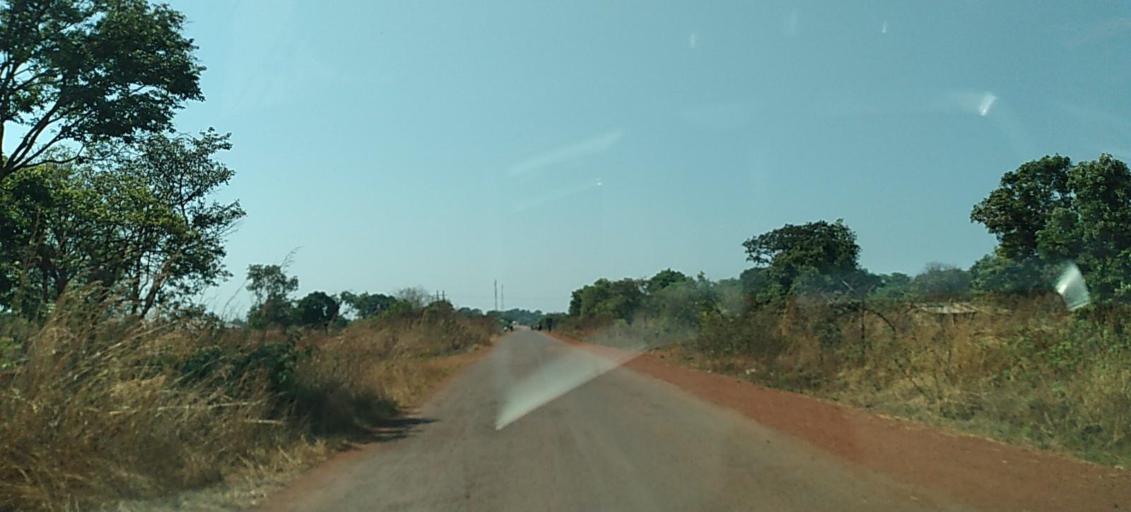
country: ZM
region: North-Western
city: Solwezi
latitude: -12.0994
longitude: 25.4906
